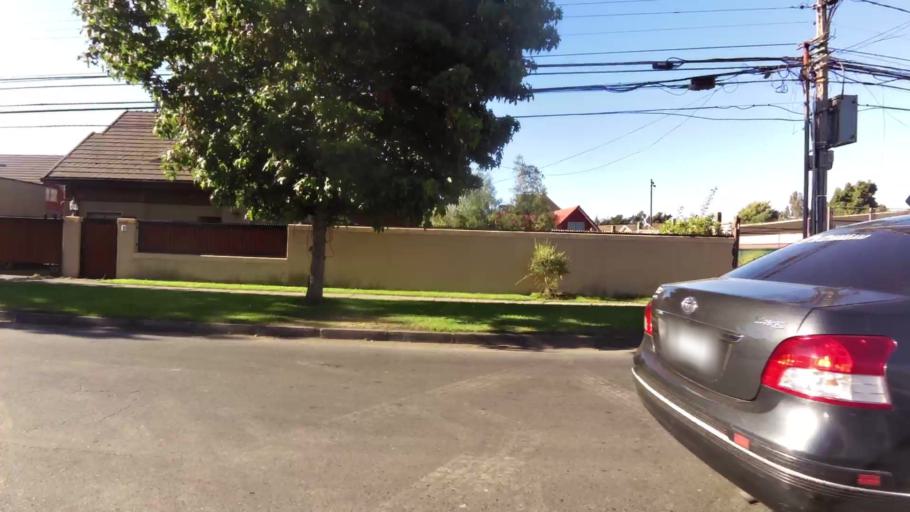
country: CL
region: Biobio
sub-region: Provincia de Concepcion
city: Concepcion
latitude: -36.8370
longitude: -73.1032
